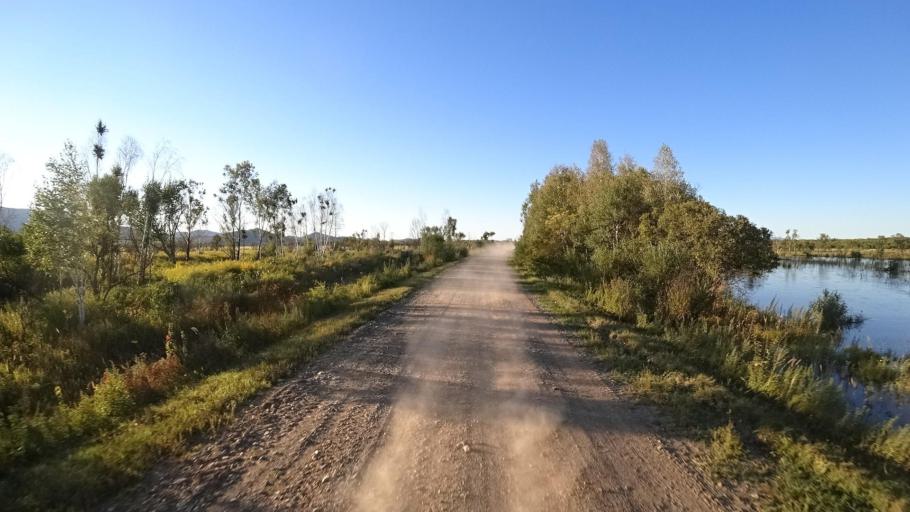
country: RU
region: Primorskiy
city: Kirovskiy
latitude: 44.8087
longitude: 133.6168
